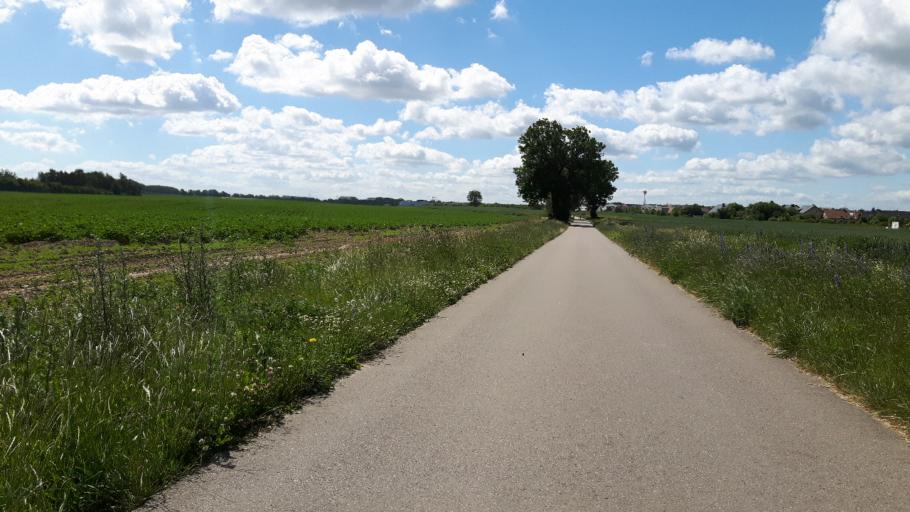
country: PL
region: Pomeranian Voivodeship
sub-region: Powiat pucki
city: Kosakowo
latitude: 54.5790
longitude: 18.4955
